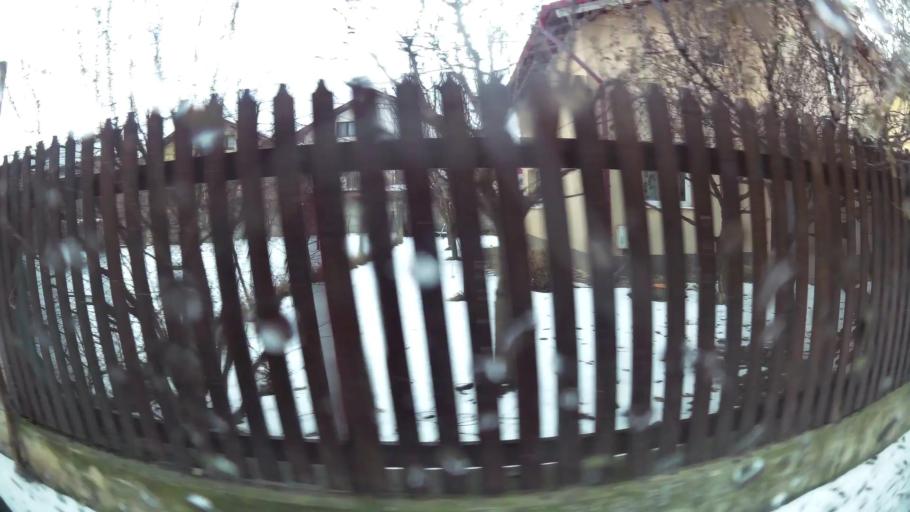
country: RO
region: Ilfov
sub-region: Comuna Chiajna
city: Rosu
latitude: 44.4034
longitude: 26.0115
